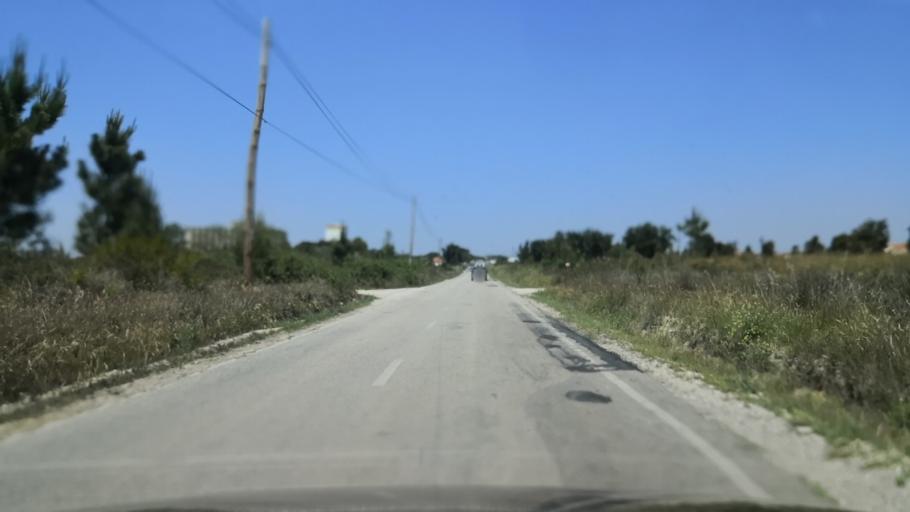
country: PT
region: Setubal
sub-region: Palmela
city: Palmela
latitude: 38.6280
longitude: -8.7467
